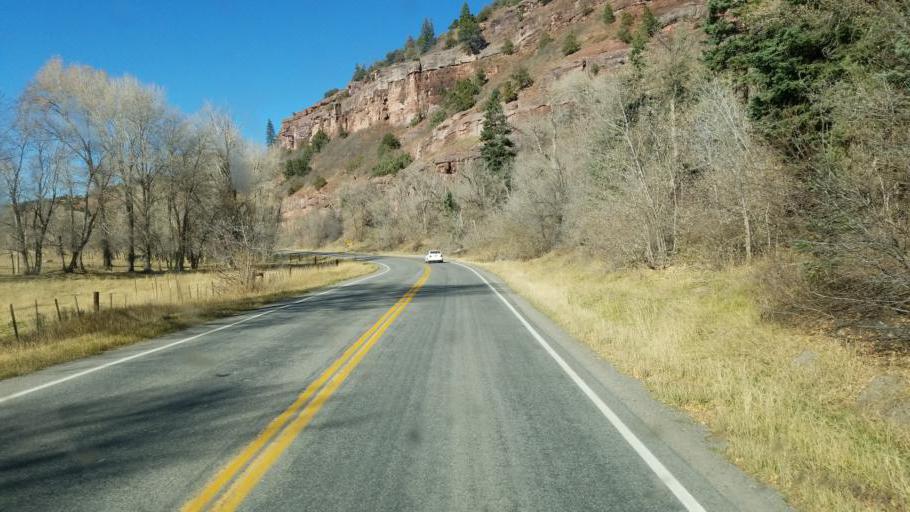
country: US
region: Colorado
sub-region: Ouray County
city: Ouray
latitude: 38.0461
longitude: -107.6819
